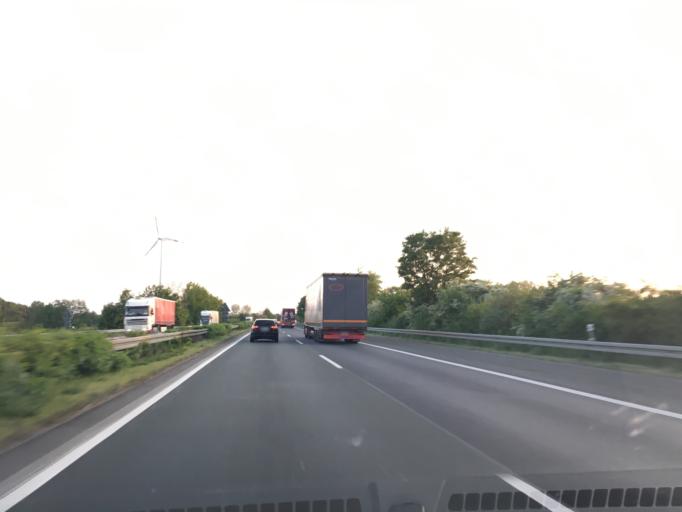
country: DE
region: North Rhine-Westphalia
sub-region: Regierungsbezirk Munster
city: Tecklenburg
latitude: 52.1893
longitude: 7.7921
